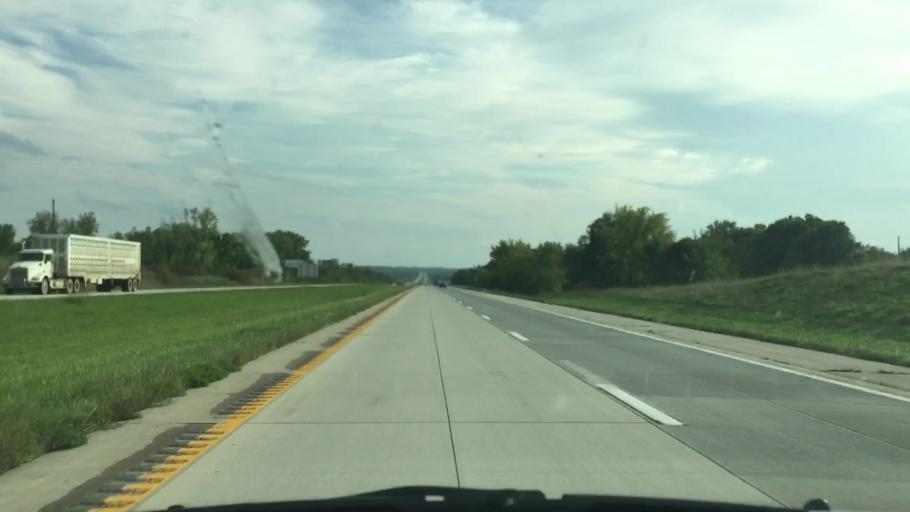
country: US
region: Missouri
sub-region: Daviess County
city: Gallatin
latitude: 40.0631
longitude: -94.0941
